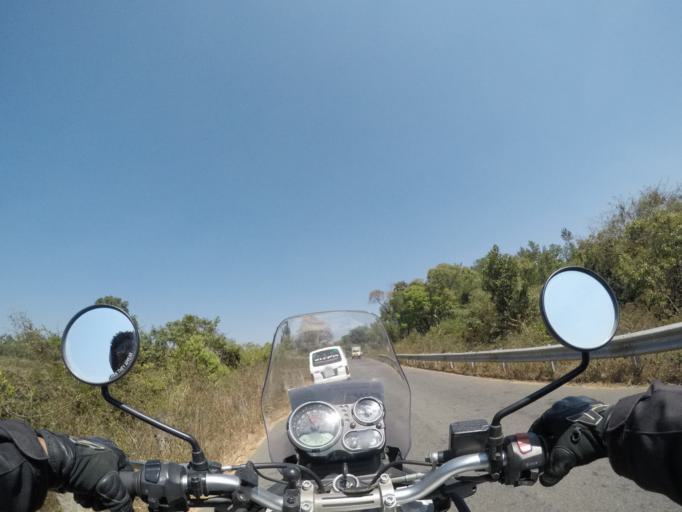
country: IN
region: Karnataka
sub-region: Chikmagalur
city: Mudigere
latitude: 13.0710
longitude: 75.6796
